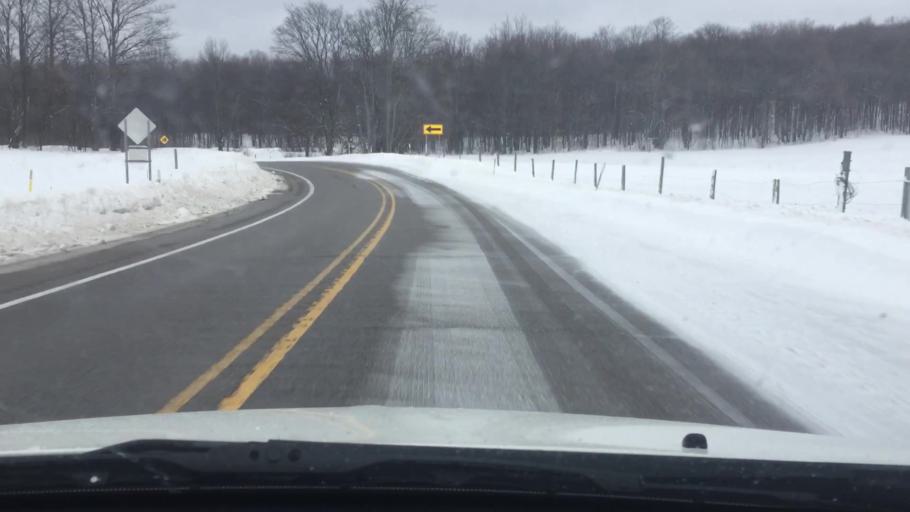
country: US
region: Michigan
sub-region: Charlevoix County
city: Boyne City
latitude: 45.0774
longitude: -84.9083
